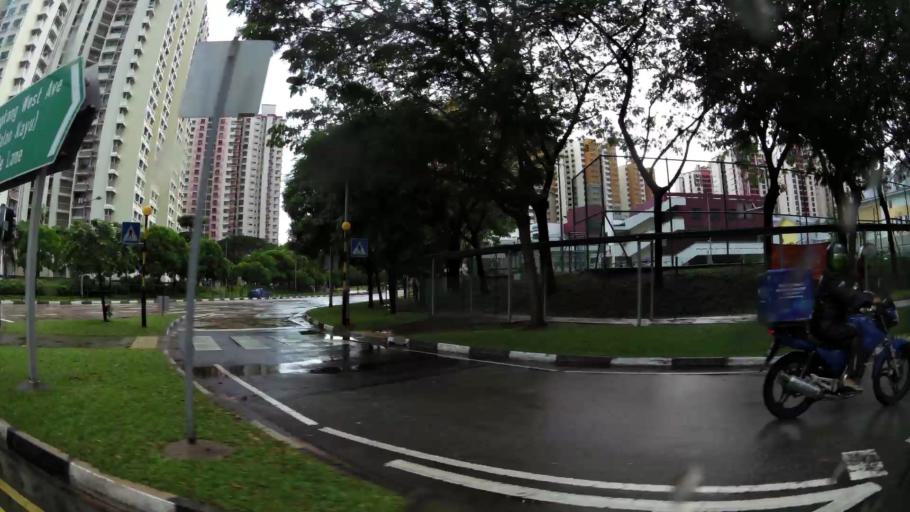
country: MY
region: Johor
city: Kampung Pasir Gudang Baru
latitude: 1.3905
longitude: 103.8753
